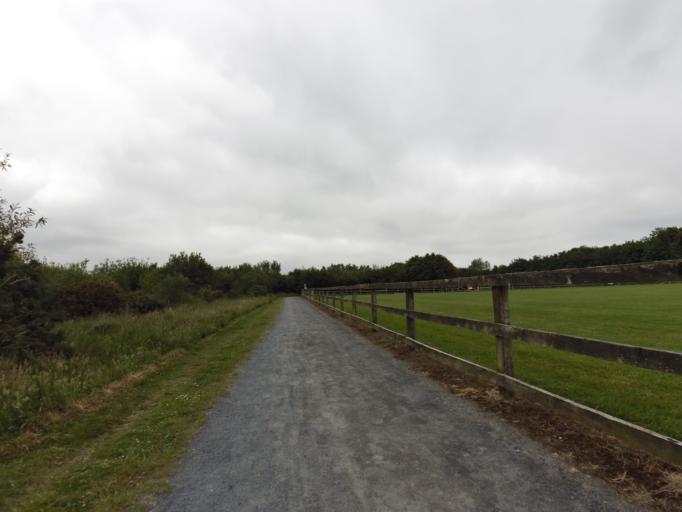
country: IE
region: Connaught
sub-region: County Galway
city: Gaillimh
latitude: 53.2960
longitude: -9.0809
